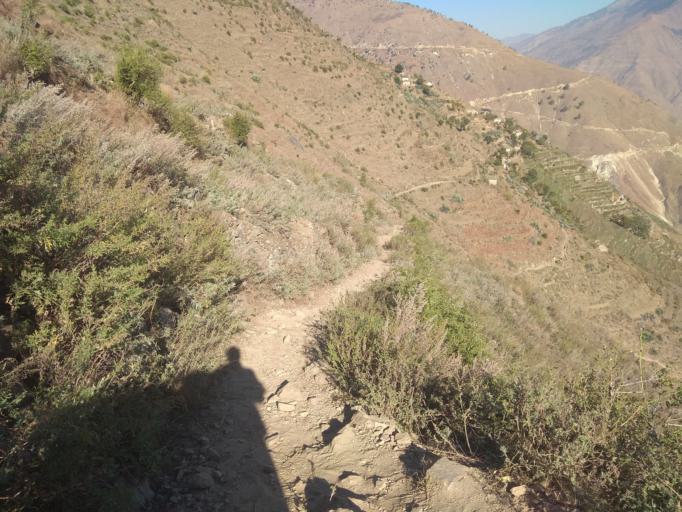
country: NP
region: Mid Western
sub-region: Karnali Zone
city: Jumla
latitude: 29.3140
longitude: 81.7417
